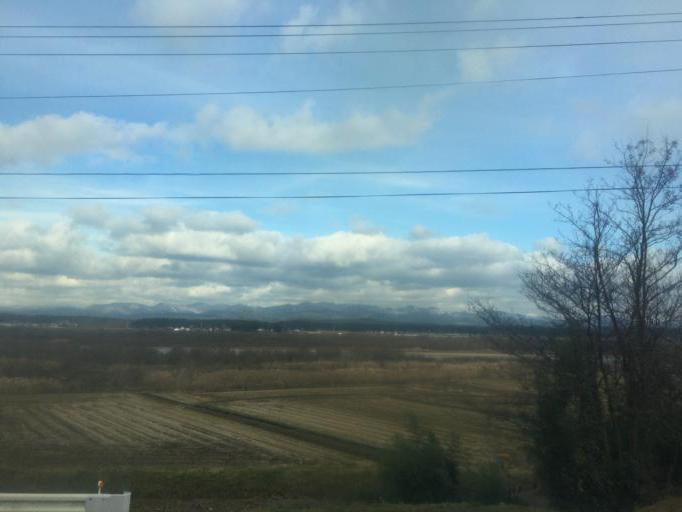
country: JP
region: Akita
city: Noshiromachi
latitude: 40.2054
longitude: 140.1141
